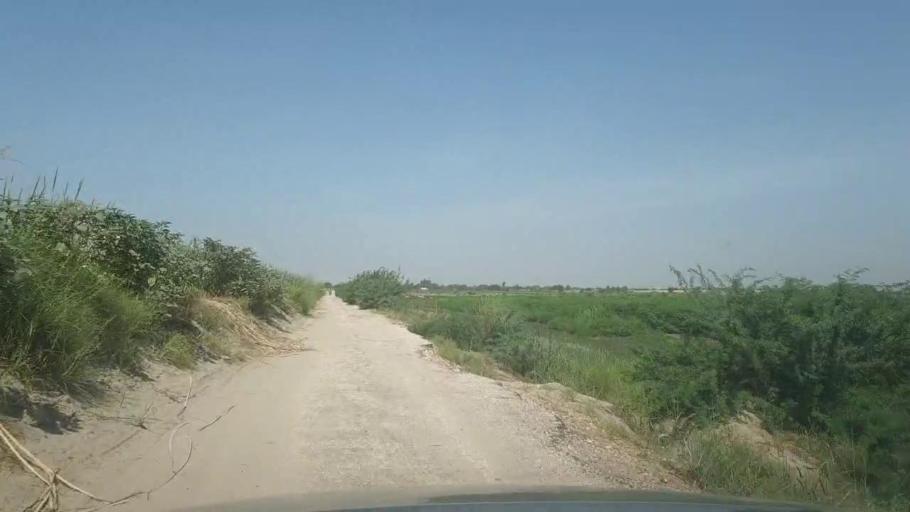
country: PK
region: Sindh
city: Khairpur
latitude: 27.3992
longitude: 69.0547
